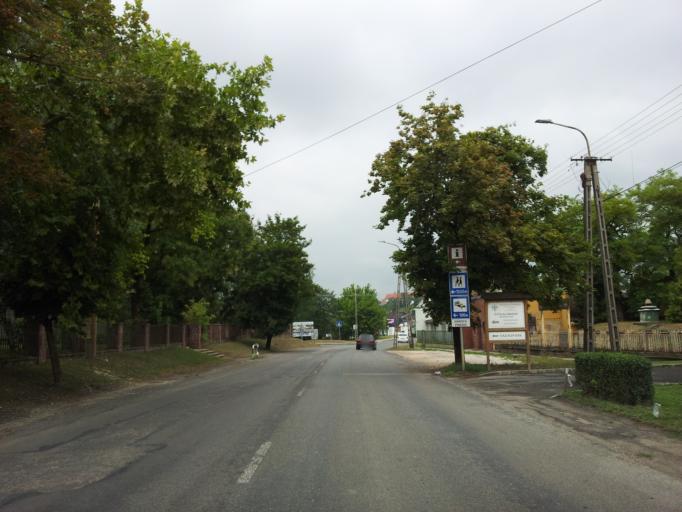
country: HU
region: Tolna
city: Tamasi
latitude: 46.6260
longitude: 18.2889
